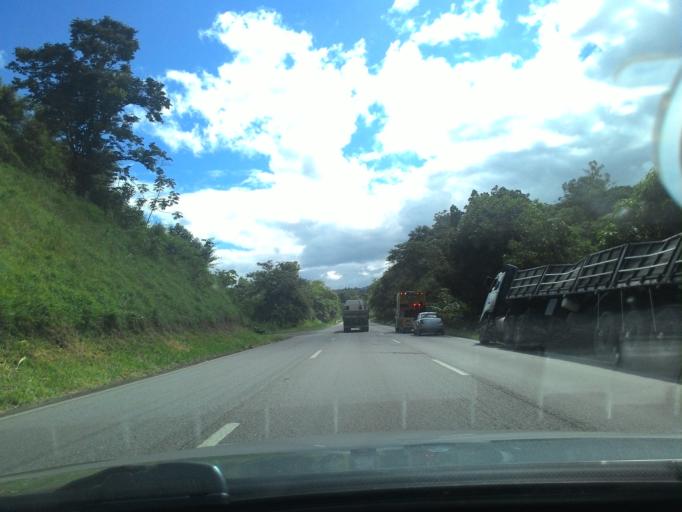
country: BR
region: Sao Paulo
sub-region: Cajati
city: Cajati
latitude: -24.7826
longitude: -48.1773
